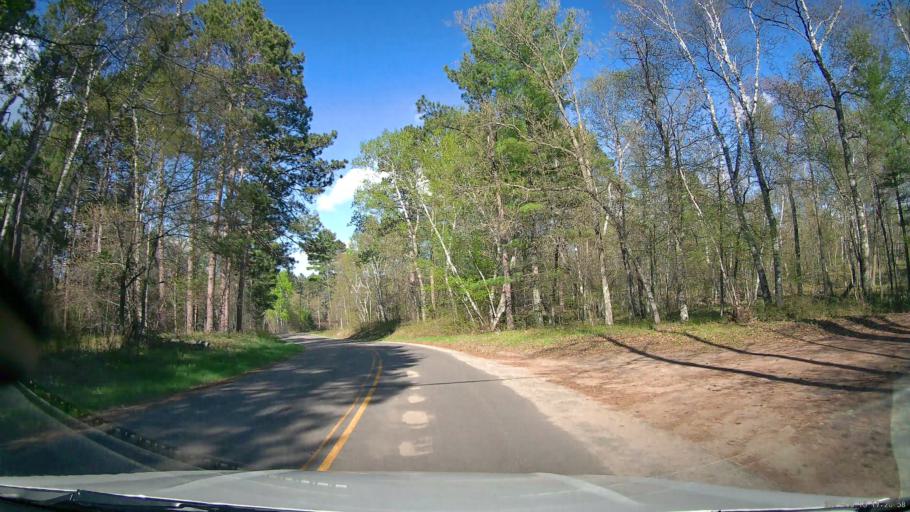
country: US
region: Minnesota
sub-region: Hubbard County
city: Park Rapids
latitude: 46.9916
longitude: -94.9630
